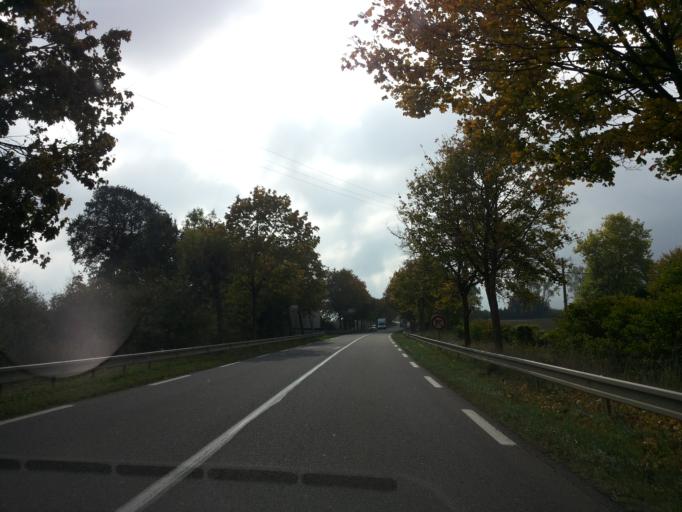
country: FR
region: Lorraine
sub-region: Departement de la Moselle
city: Solgne
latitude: 48.9651
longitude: 6.2993
